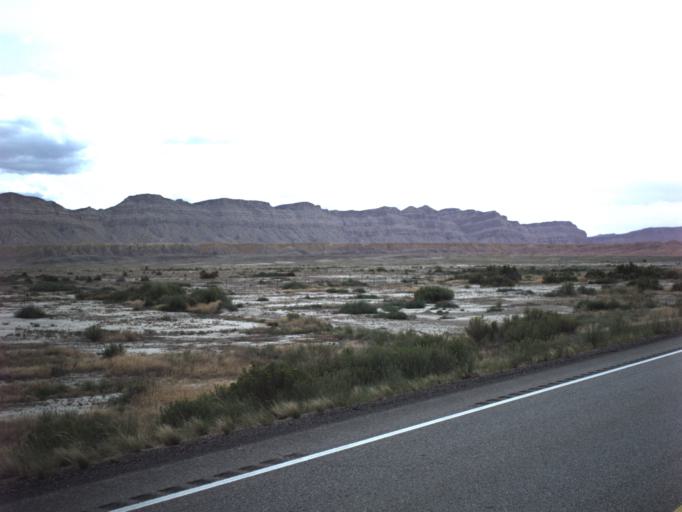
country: US
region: Utah
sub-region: Carbon County
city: East Carbon City
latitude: 39.3283
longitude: -110.3677
